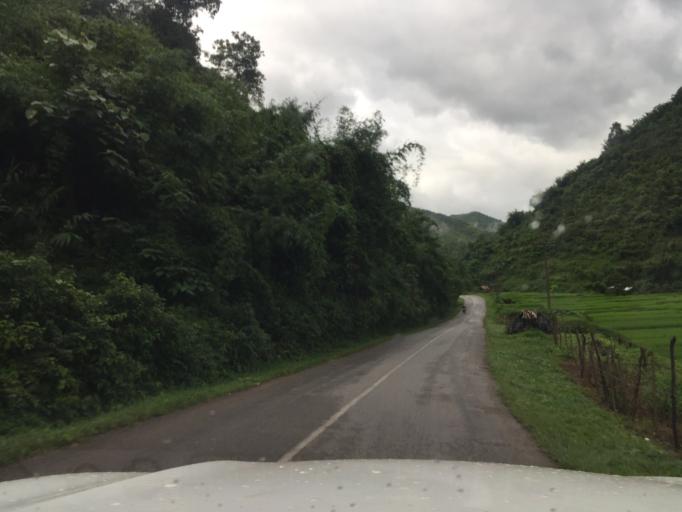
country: LA
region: Oudomxai
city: Muang La
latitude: 20.8220
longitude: 102.0963
